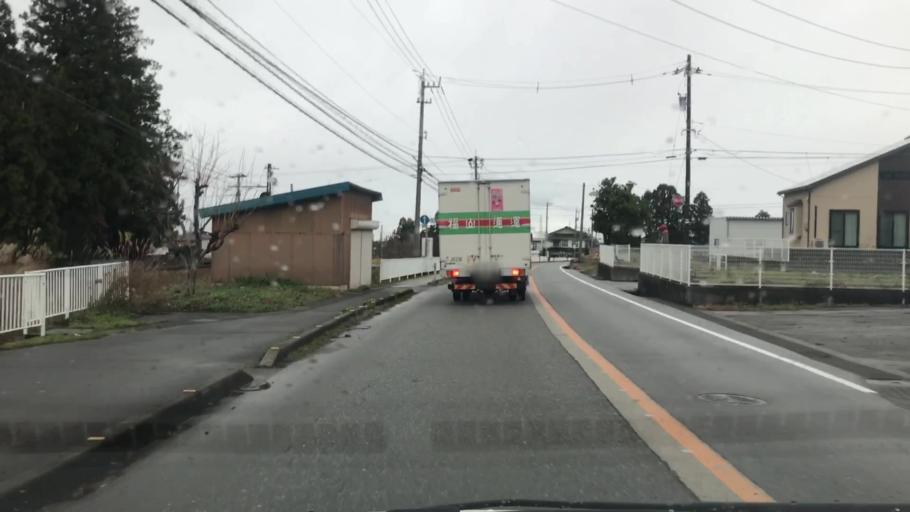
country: JP
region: Toyama
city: Kamiichi
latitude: 36.6045
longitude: 137.3207
